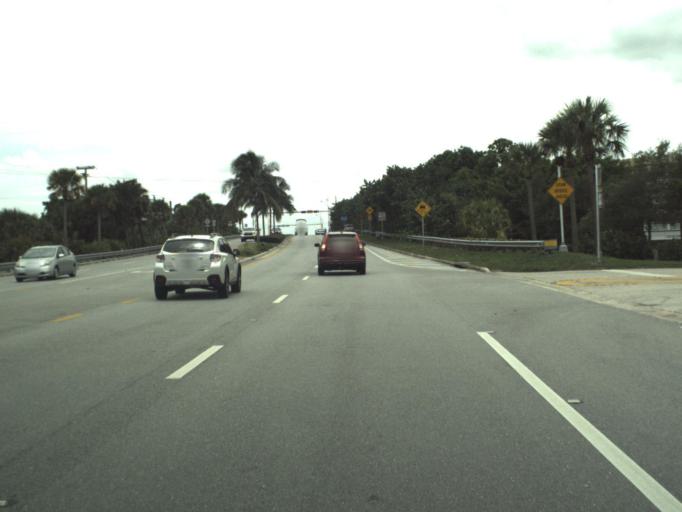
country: US
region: Florida
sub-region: Palm Beach County
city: Jupiter
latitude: 26.9504
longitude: -80.0853
